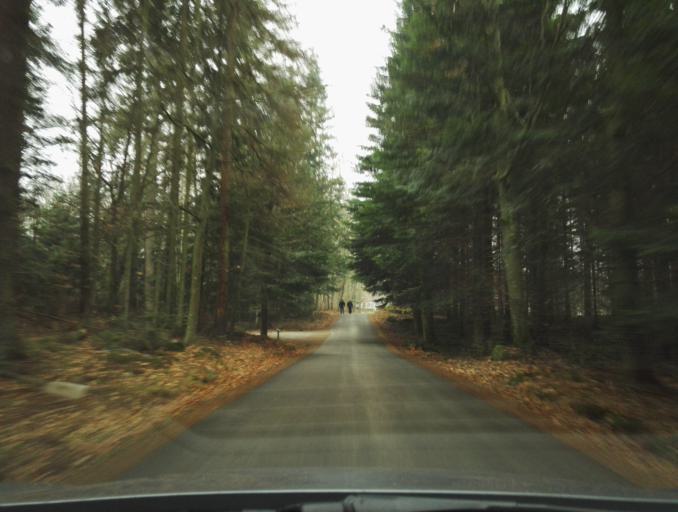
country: SE
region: Kronoberg
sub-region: Vaxjo Kommun
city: Vaexjoe
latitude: 56.9420
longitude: 14.8023
